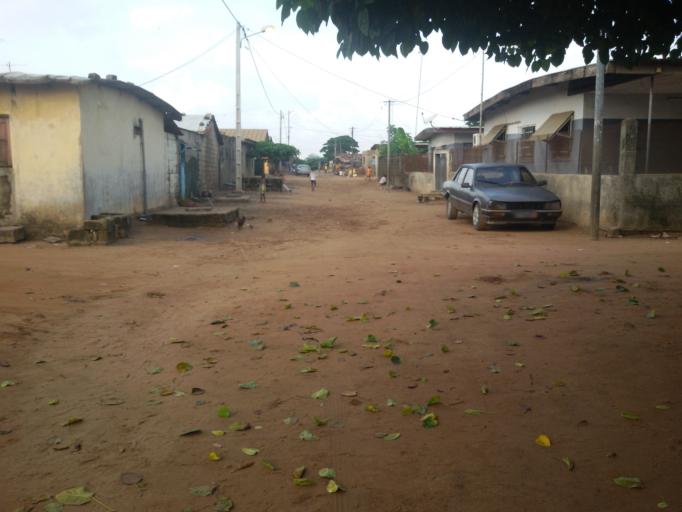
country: CI
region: Sud-Comoe
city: Grand-Bassam
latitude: 5.2062
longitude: -3.7321
